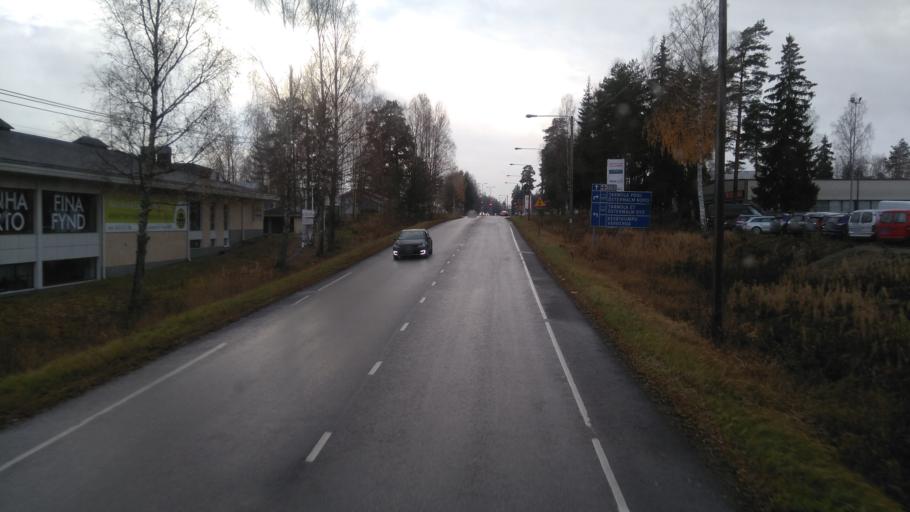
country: FI
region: Uusimaa
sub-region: Porvoo
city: Porvoo
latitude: 60.4048
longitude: 25.6903
